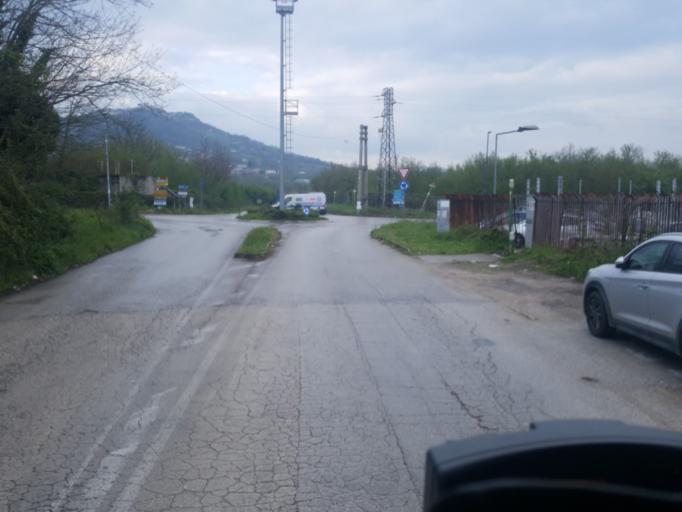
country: IT
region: Campania
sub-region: Provincia di Avellino
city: Atripalda
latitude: 40.9379
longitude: 14.8207
